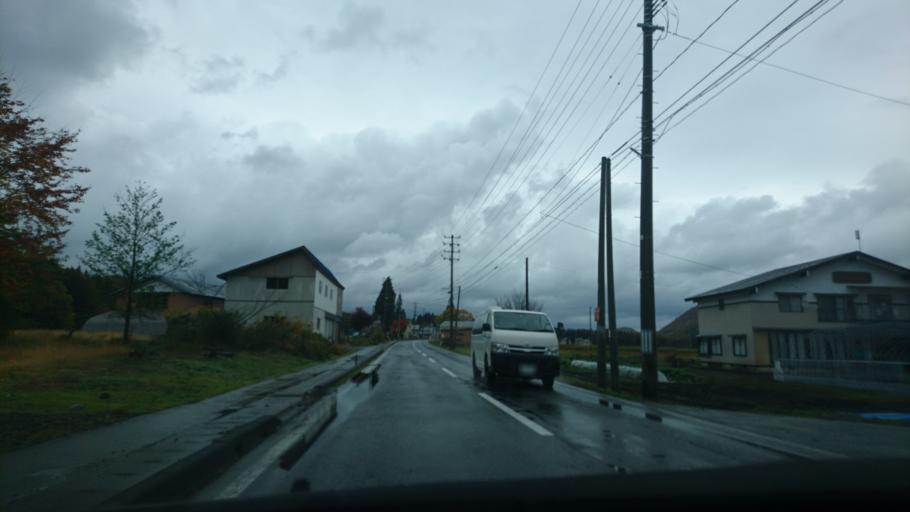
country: JP
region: Akita
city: Yokotemachi
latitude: 39.3645
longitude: 140.7618
